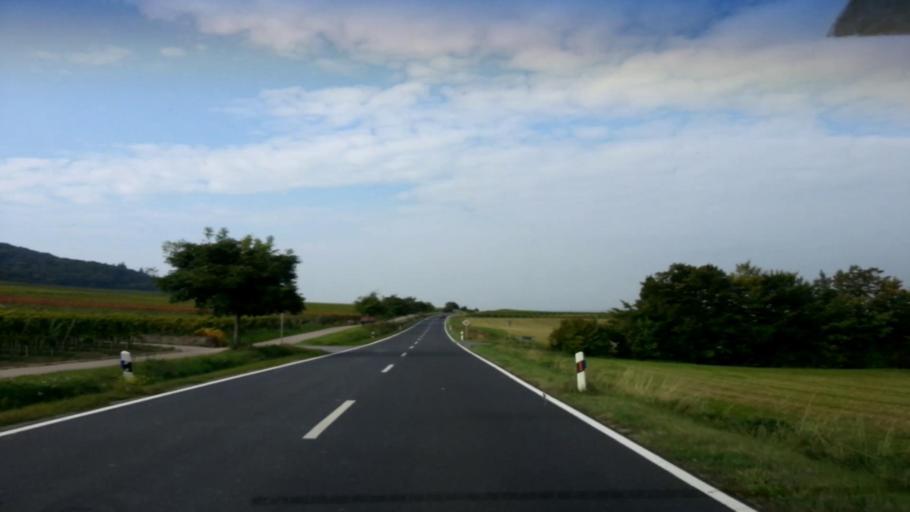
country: DE
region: Bavaria
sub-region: Regierungsbezirk Unterfranken
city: Wiesenbronn
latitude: 49.7359
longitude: 10.2825
